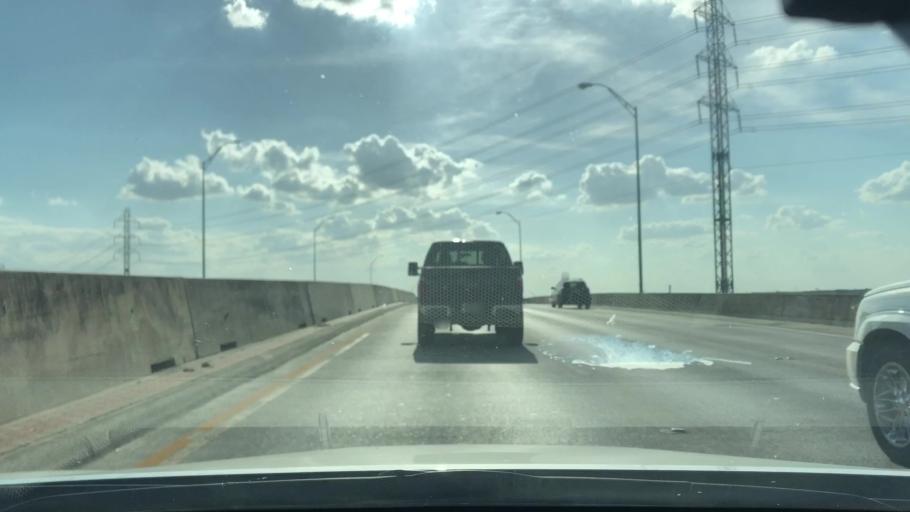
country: US
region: Texas
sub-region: Bexar County
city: Windcrest
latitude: 29.5458
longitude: -98.4346
